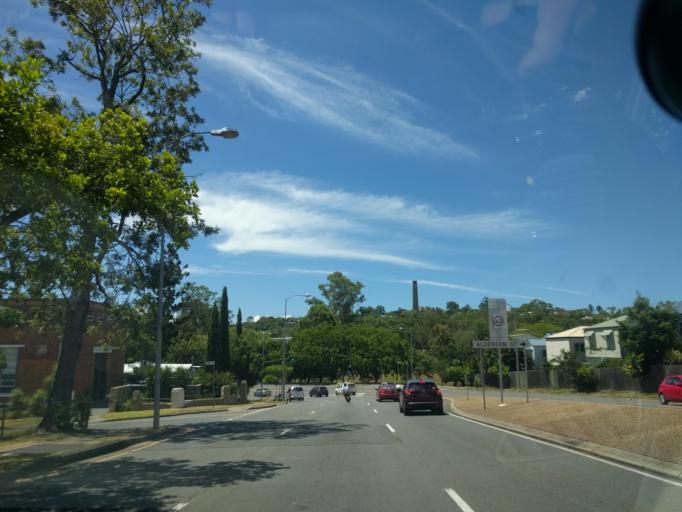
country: AU
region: Queensland
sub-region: Brisbane
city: Grange
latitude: -27.4309
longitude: 153.0052
